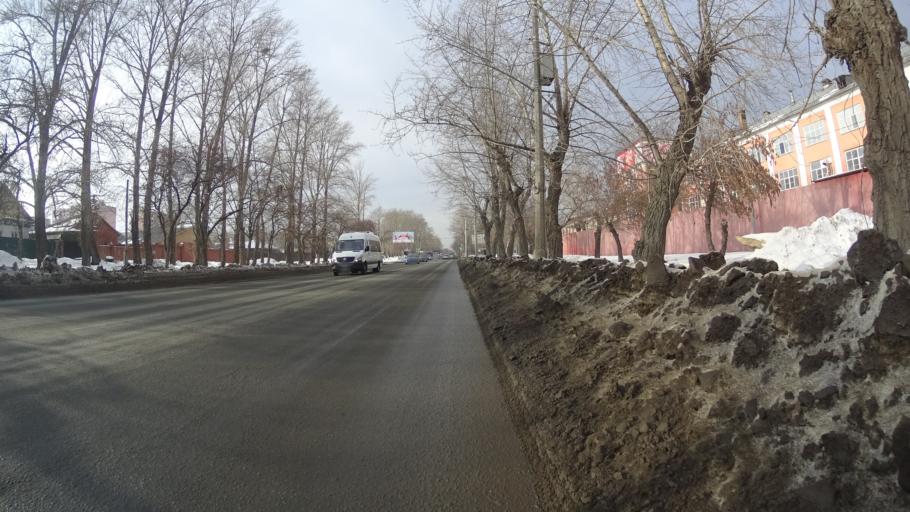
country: RU
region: Chelyabinsk
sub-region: Gorod Chelyabinsk
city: Chelyabinsk
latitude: 55.1231
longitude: 61.3748
